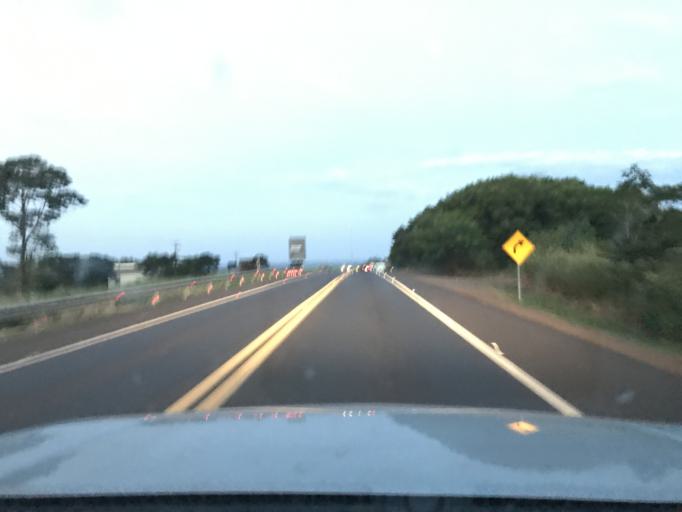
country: PY
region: Canindeyu
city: Salto del Guaira
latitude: -24.0117
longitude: -54.3032
